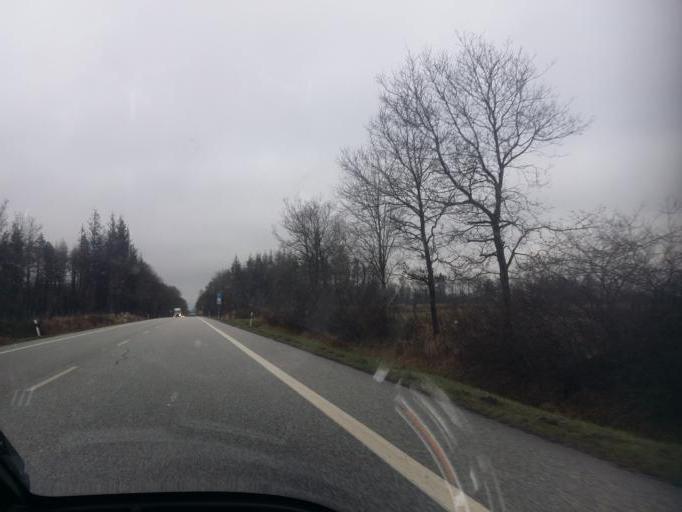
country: DE
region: Schleswig-Holstein
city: Bordelum
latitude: 54.6543
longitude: 8.9483
